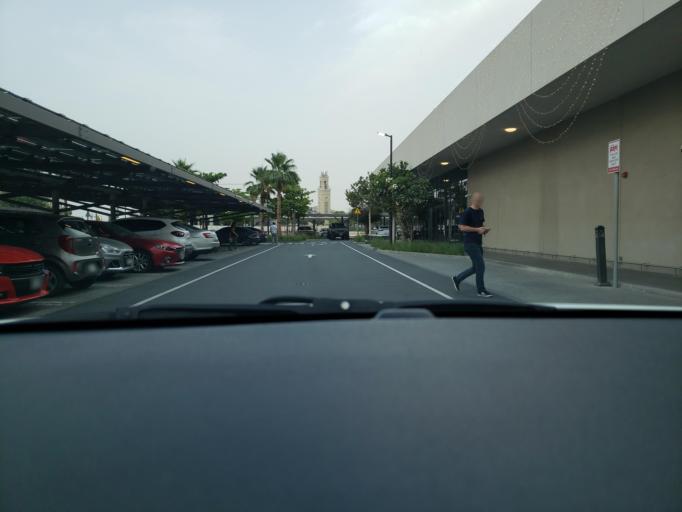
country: AE
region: Dubai
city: Dubai
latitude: 25.0418
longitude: 55.2294
